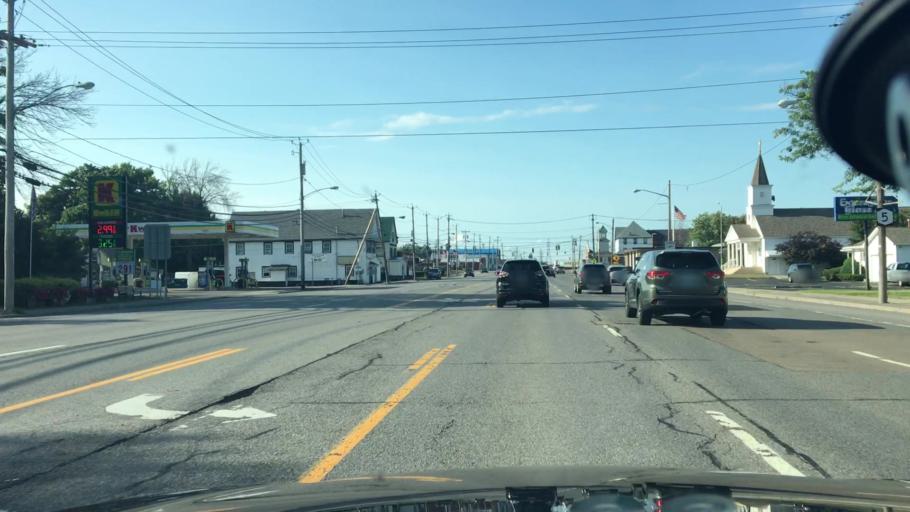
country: US
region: New York
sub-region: Erie County
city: Blasdell
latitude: 42.7949
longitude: -78.8468
